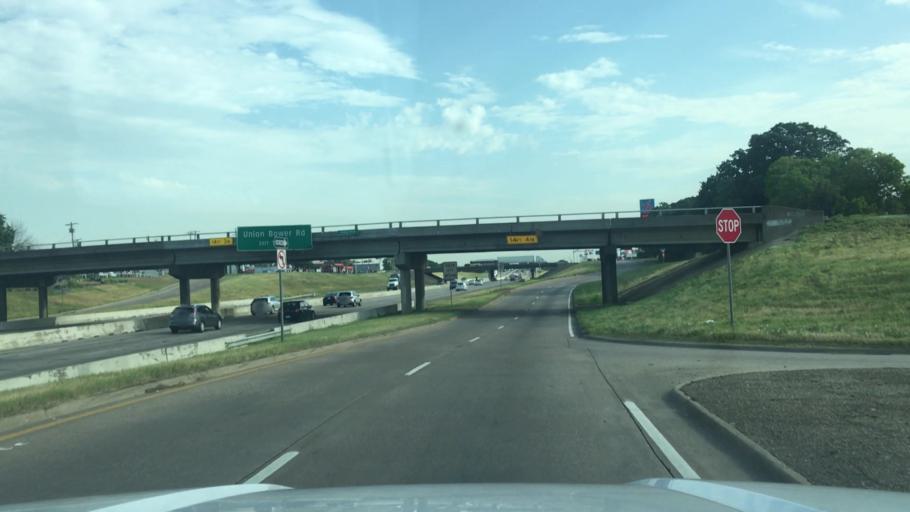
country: US
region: Texas
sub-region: Dallas County
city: Irving
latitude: 32.8061
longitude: -96.9213
